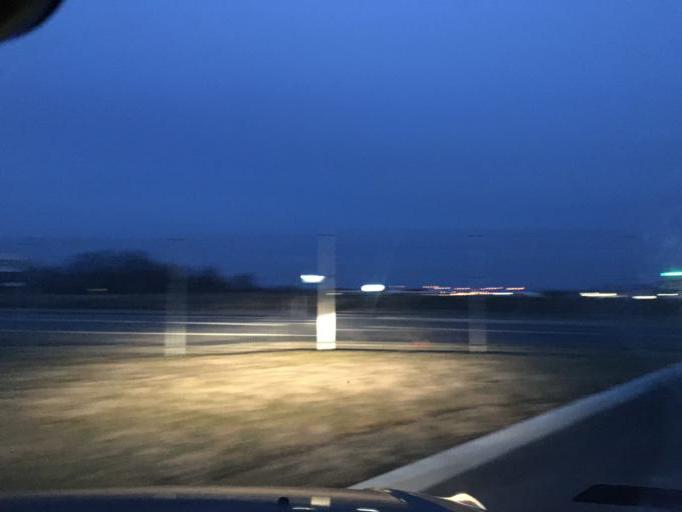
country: HU
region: Csongrad
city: Szatymaz
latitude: 46.2905
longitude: 20.0842
